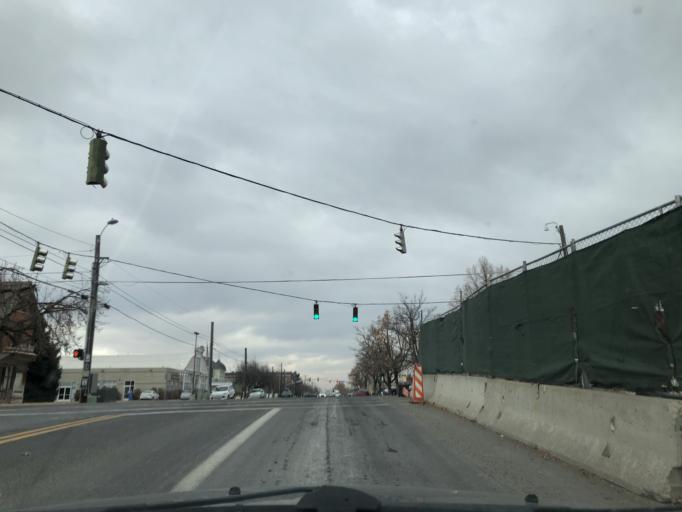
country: US
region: Utah
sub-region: Cache County
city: Logan
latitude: 41.7293
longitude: -111.8377
